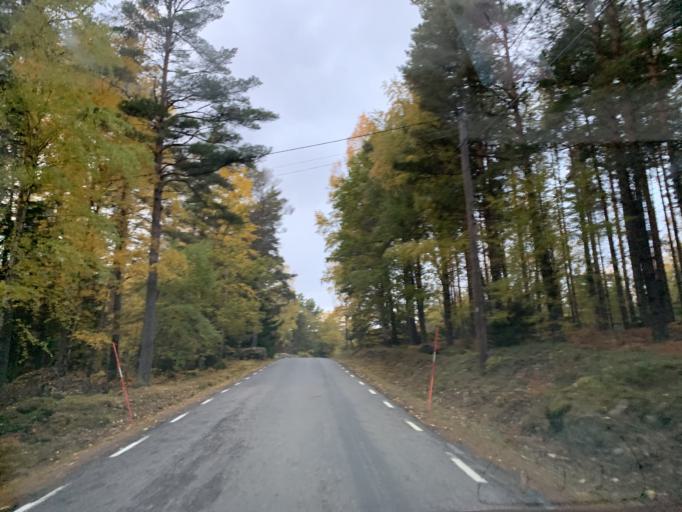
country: SE
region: Stockholm
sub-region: Nynashamns Kommun
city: Osmo
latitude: 58.9179
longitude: 17.7784
